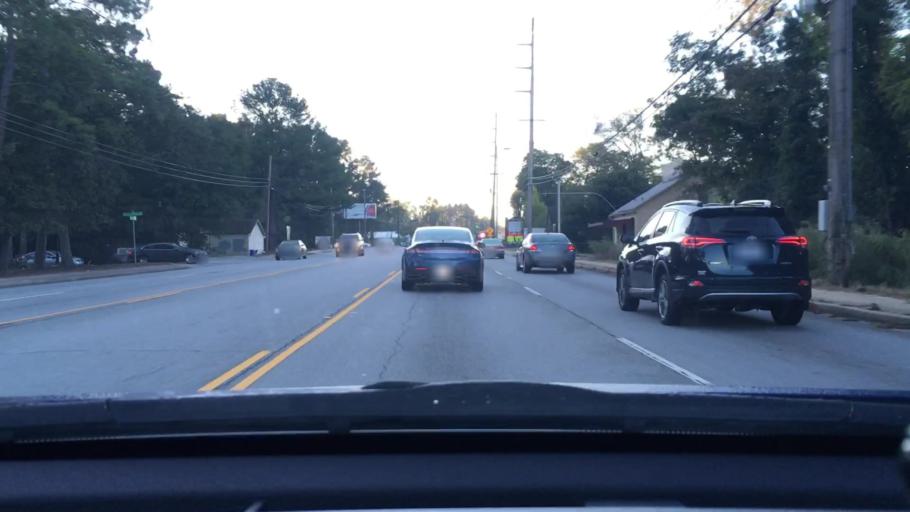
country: US
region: South Carolina
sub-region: Lexington County
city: Saint Andrews
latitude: 34.0587
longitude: -81.1121
